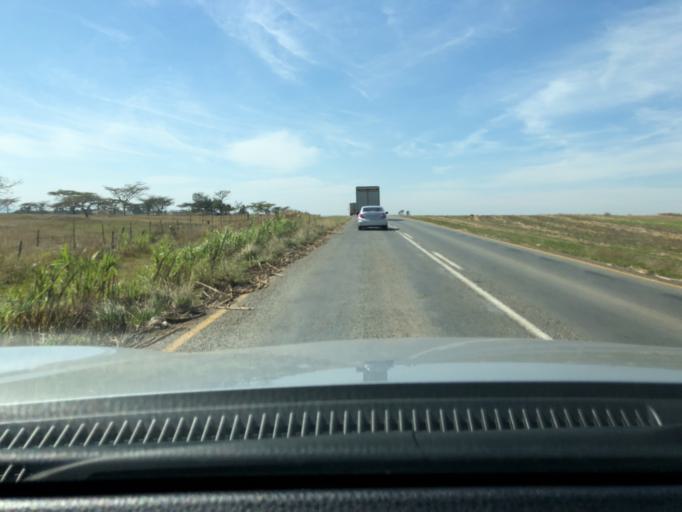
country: ZA
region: KwaZulu-Natal
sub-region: uMgungundlovu District Municipality
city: Camperdown
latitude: -29.7309
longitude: 30.4549
